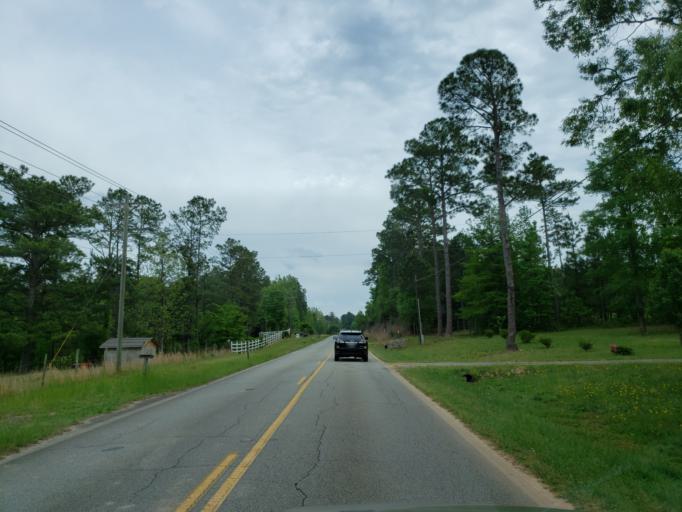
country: US
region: Georgia
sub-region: Bibb County
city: West Point
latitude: 32.8136
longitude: -83.8498
